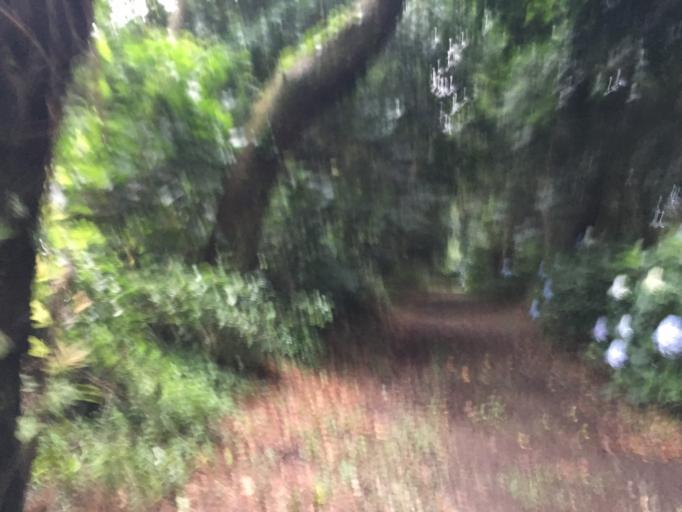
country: JP
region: Aichi
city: Ishiki
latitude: 34.7296
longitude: 137.0450
